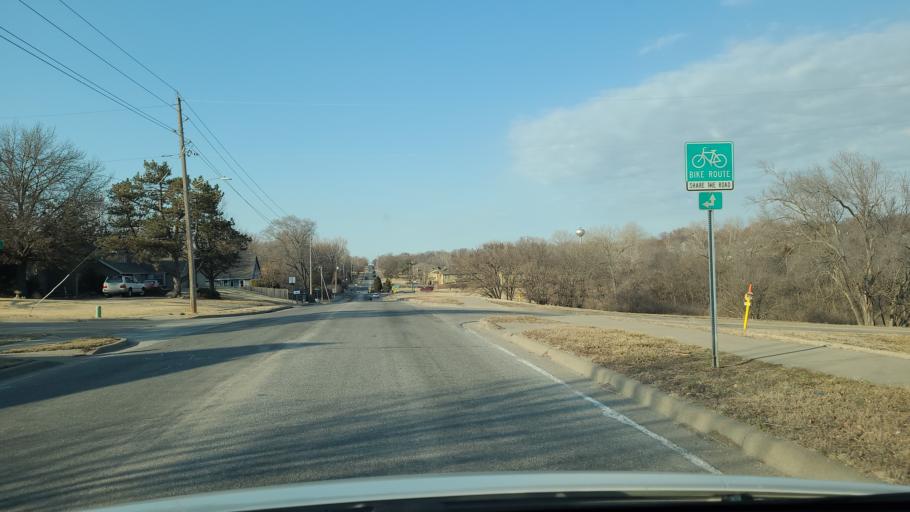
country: US
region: Kansas
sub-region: Douglas County
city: Lawrence
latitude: 38.9619
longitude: -95.2883
